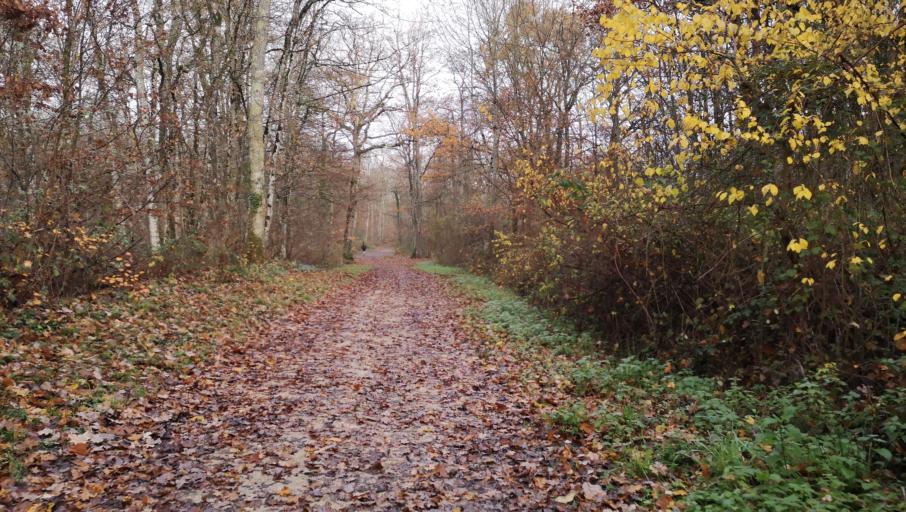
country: FR
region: Centre
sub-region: Departement du Loiret
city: Semoy
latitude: 47.9423
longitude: 1.9603
